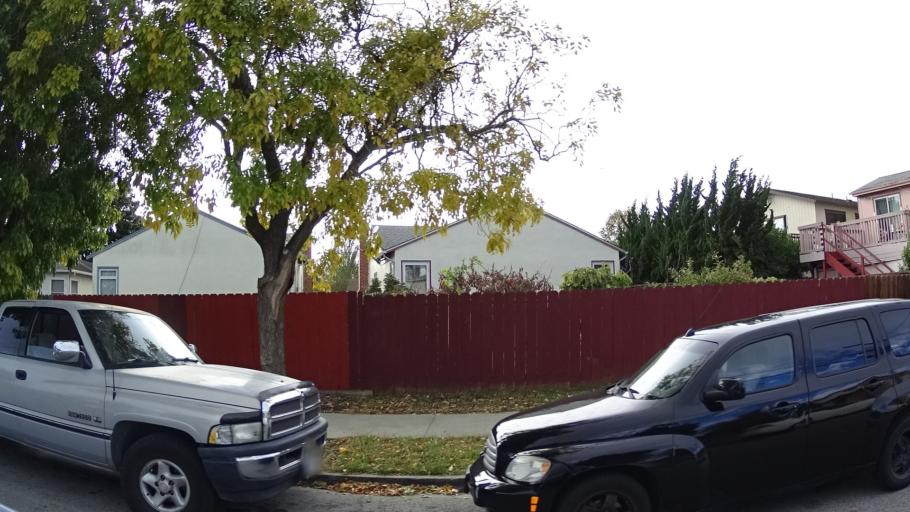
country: US
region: California
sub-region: San Mateo County
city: San Bruno
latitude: 37.6292
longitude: -122.4052
